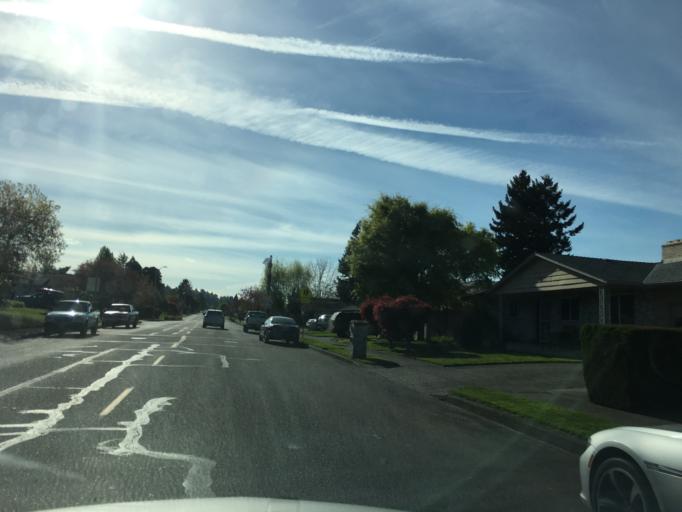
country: US
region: Oregon
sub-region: Multnomah County
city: Lents
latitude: 45.5481
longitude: -122.5259
